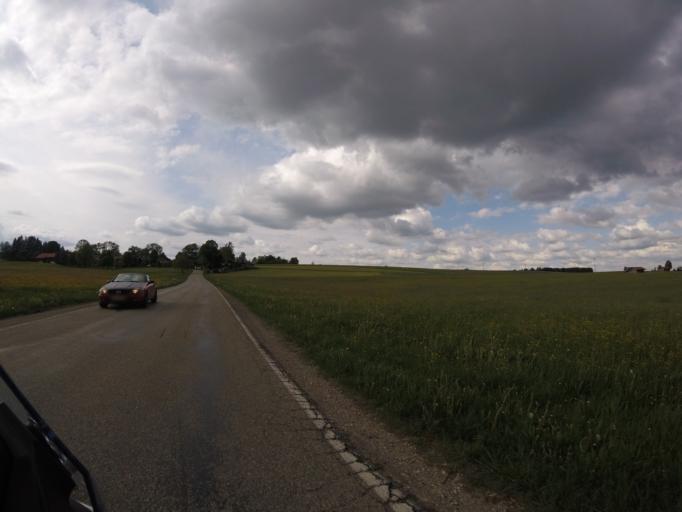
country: DE
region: Bavaria
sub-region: Upper Bavaria
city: Reichertshausen
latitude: 47.8642
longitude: 11.5444
